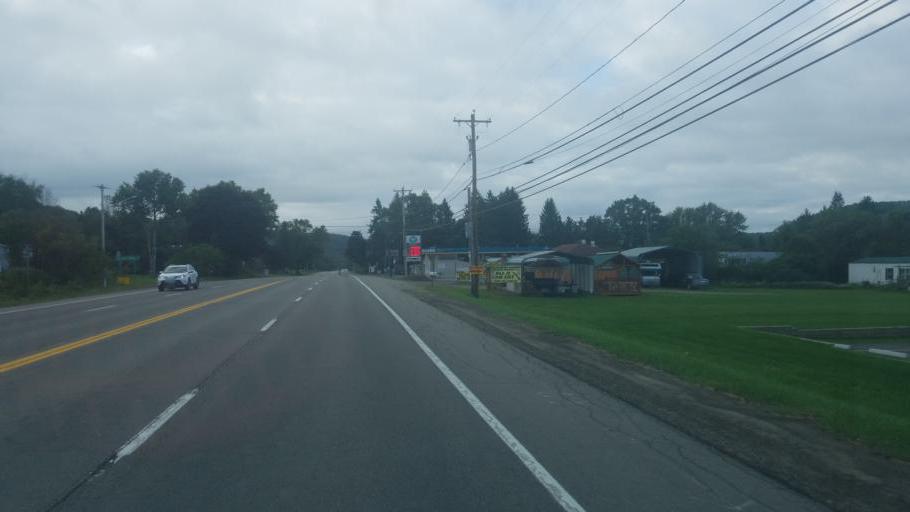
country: US
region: New York
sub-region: Cattaraugus County
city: Weston Mills
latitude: 42.1522
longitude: -78.3983
